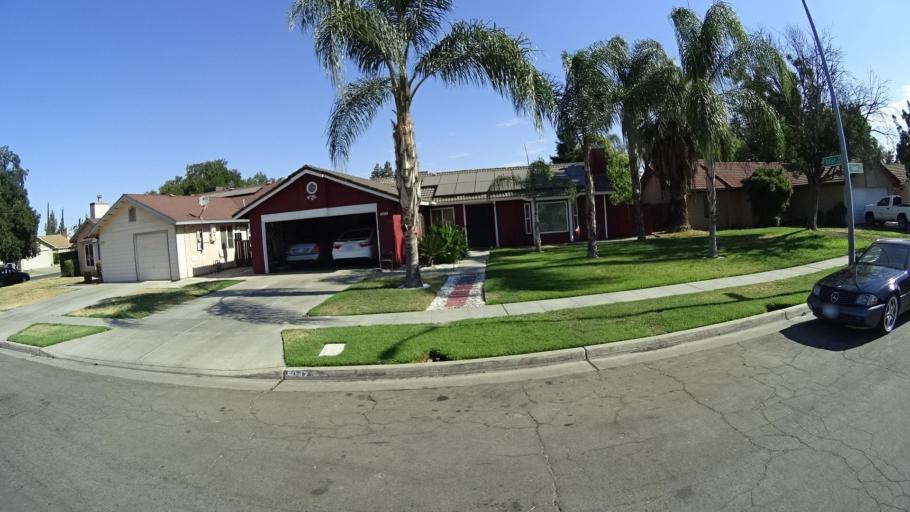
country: US
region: California
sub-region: Fresno County
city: Sunnyside
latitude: 36.7151
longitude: -119.7255
